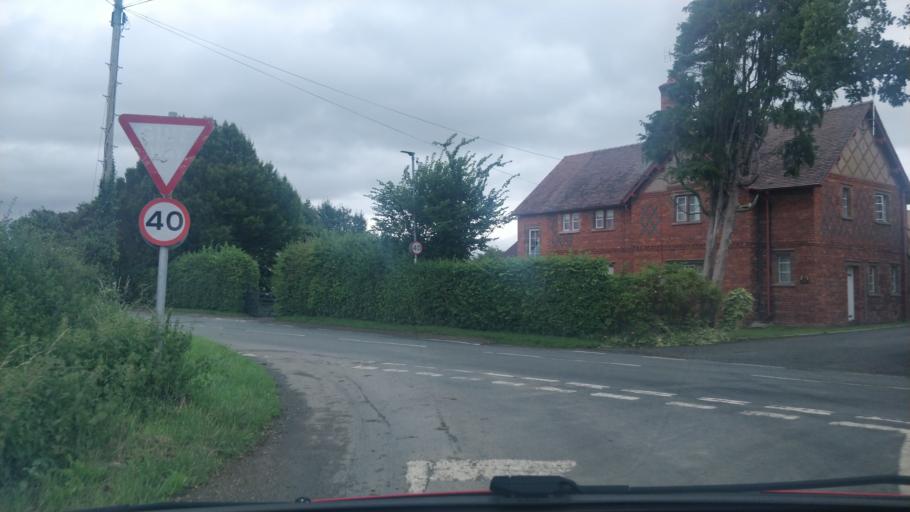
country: GB
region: Wales
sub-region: Wrexham
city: Rossett
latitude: 53.1521
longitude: -2.9626
